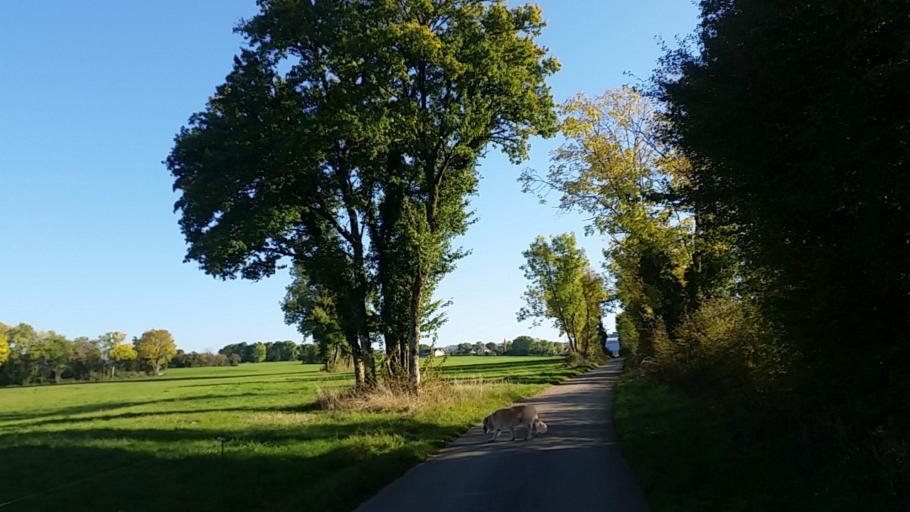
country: FR
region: Franche-Comte
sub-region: Departement du Doubs
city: Ornans
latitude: 47.0470
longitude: 6.0692
